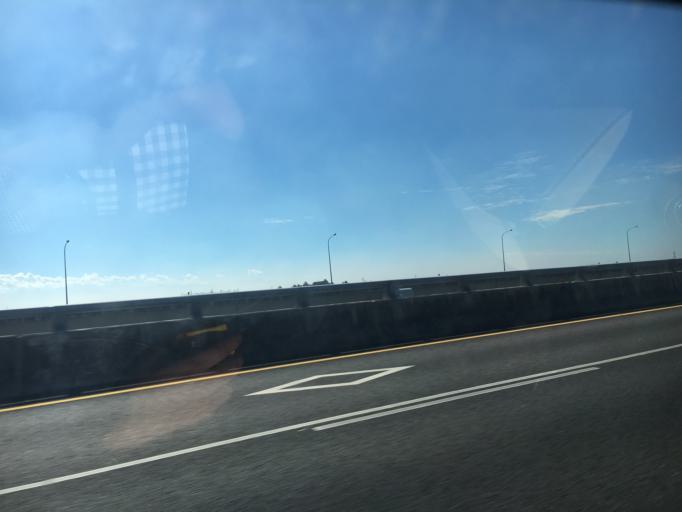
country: TW
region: Taiwan
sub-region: Taoyuan
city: Taoyuan
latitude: 25.0654
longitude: 121.3592
